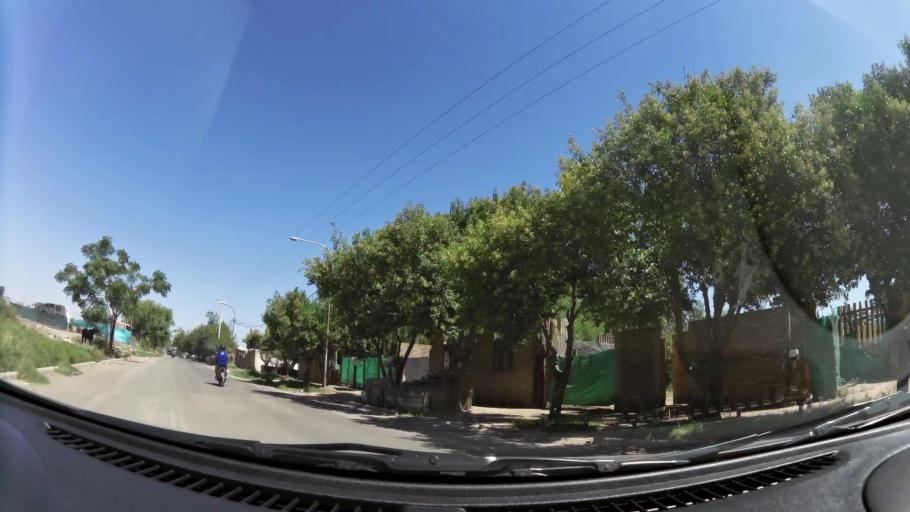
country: AR
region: Mendoza
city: Villa Nueva
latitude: -32.8744
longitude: -68.7861
